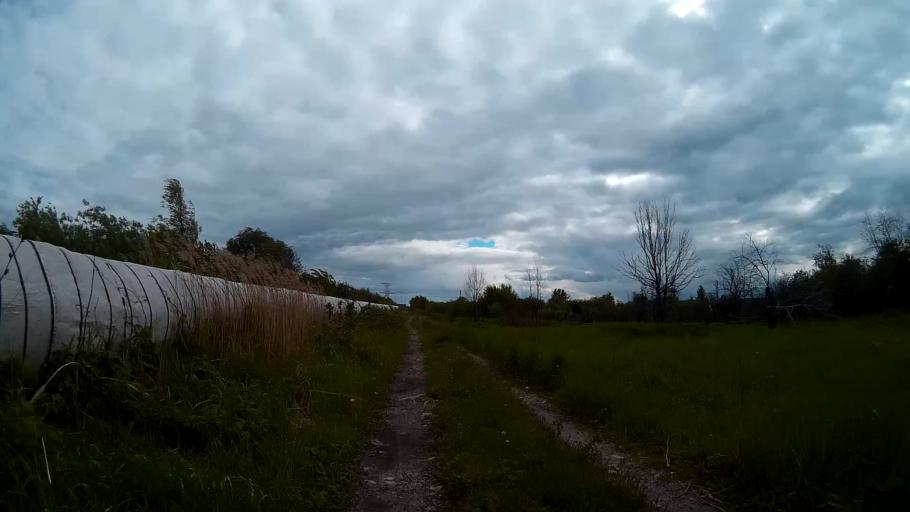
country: RU
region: Ulyanovsk
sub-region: Ulyanovskiy Rayon
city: Ulyanovsk
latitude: 54.2441
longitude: 48.2998
